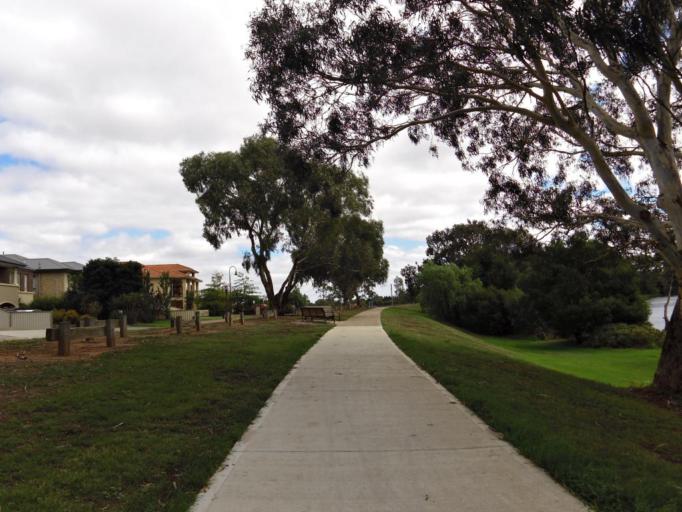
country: AU
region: Victoria
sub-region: Wyndham
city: Tarneit
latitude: -37.8799
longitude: 144.6498
